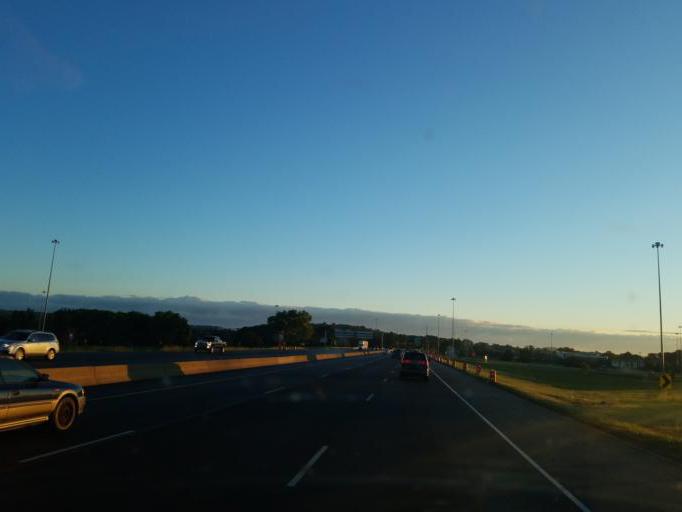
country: US
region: Ohio
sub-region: Summit County
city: Montrose-Ghent
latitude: 41.1325
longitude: -81.6512
